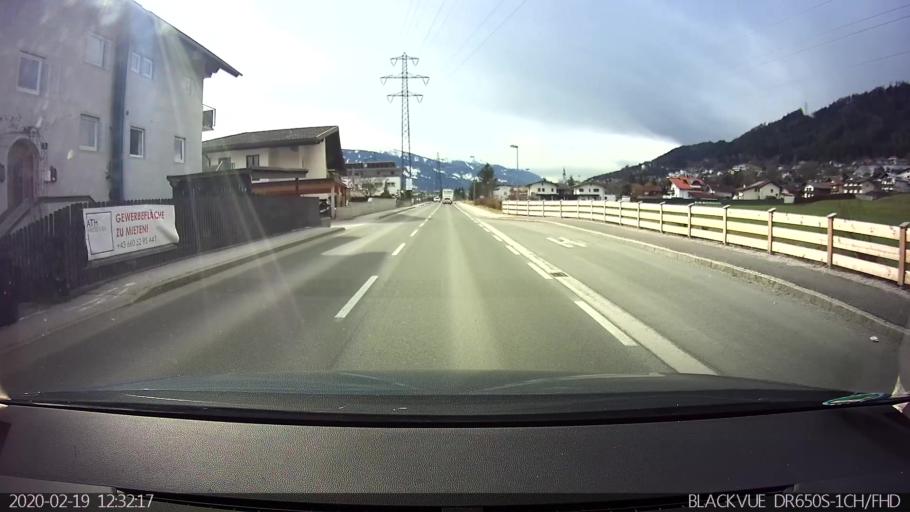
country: AT
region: Tyrol
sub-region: Politischer Bezirk Schwaz
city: Schwaz
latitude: 47.3471
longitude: 11.6956
